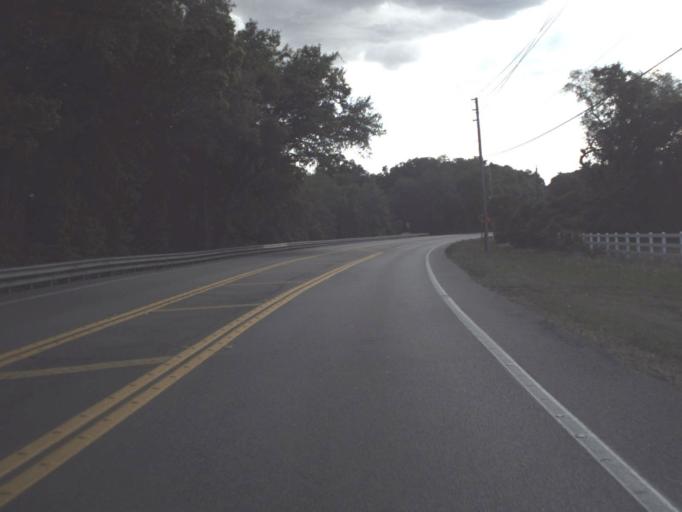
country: US
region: Florida
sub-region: Lake County
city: Mount Plymouth
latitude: 28.8049
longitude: -81.5728
